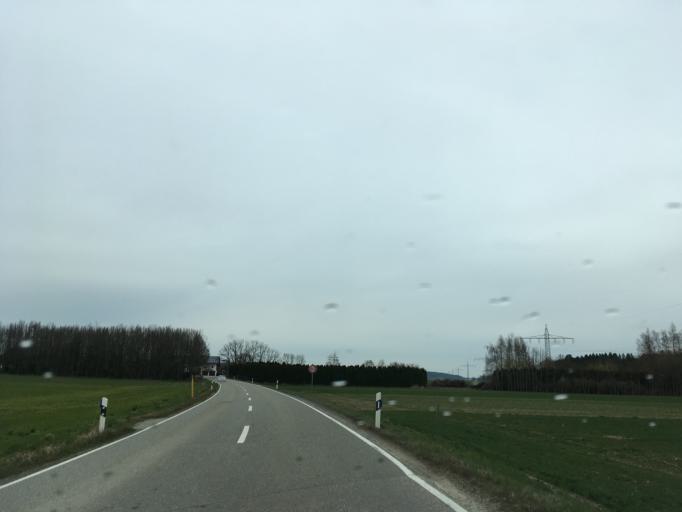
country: DE
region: Bavaria
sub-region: Upper Bavaria
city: Schnaitsee
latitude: 48.0949
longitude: 12.4089
